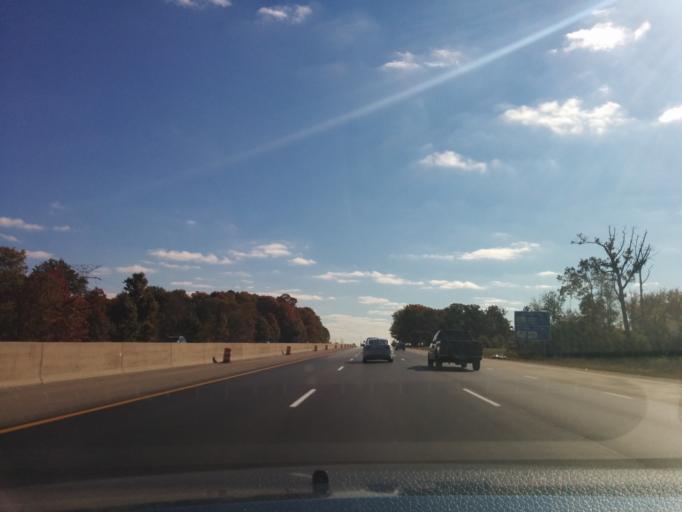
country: US
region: Michigan
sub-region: Oakland County
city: Novi
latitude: 42.4918
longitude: -83.5073
